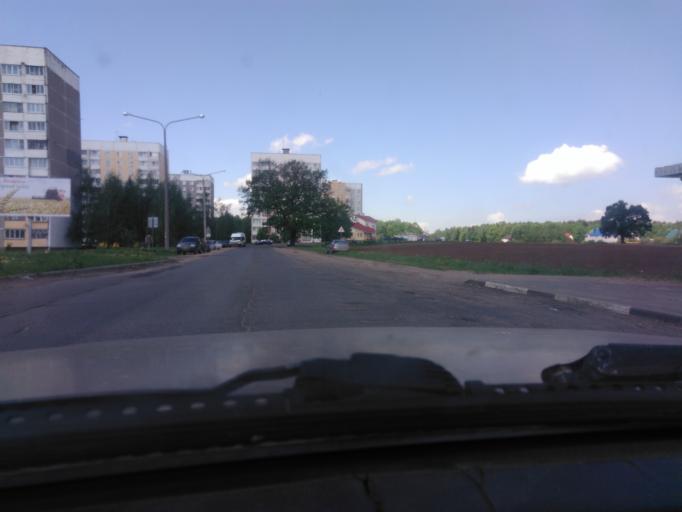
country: BY
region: Mogilev
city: Palykavichy Pyershyya
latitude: 53.9498
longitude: 30.3742
